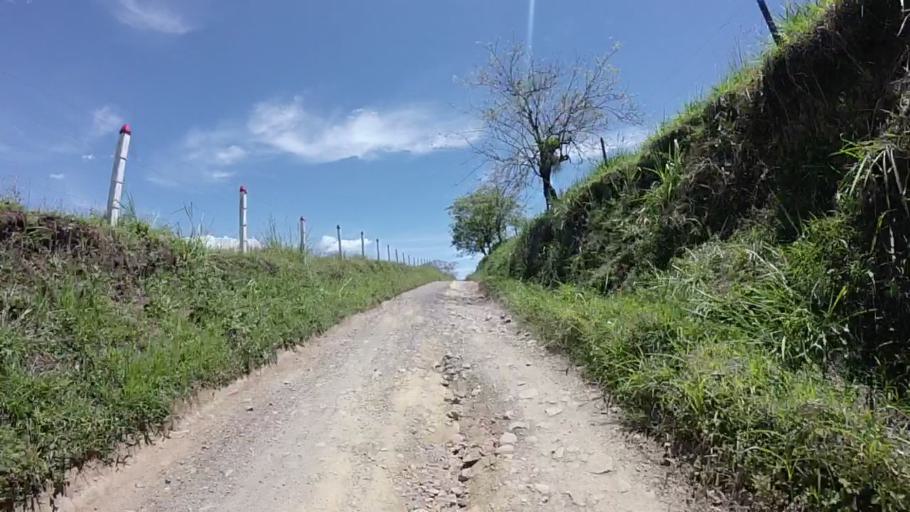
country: CO
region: Valle del Cauca
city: Alcala
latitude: 4.7144
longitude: -75.7975
